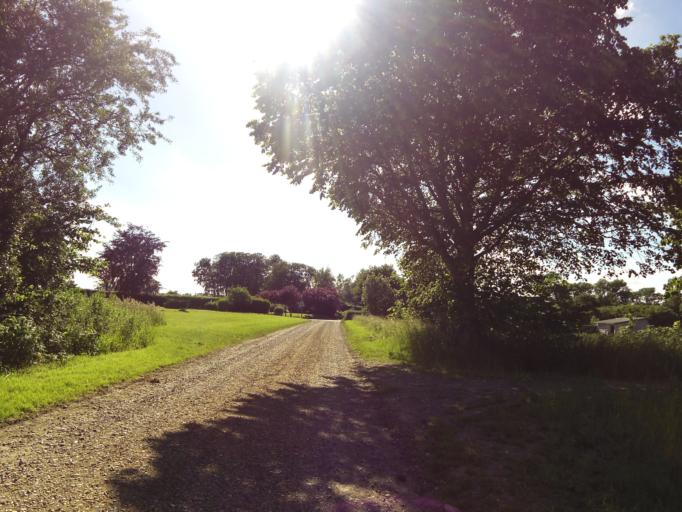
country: DK
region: South Denmark
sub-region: Tonder Kommune
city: Toftlund
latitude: 55.1053
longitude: 9.1632
